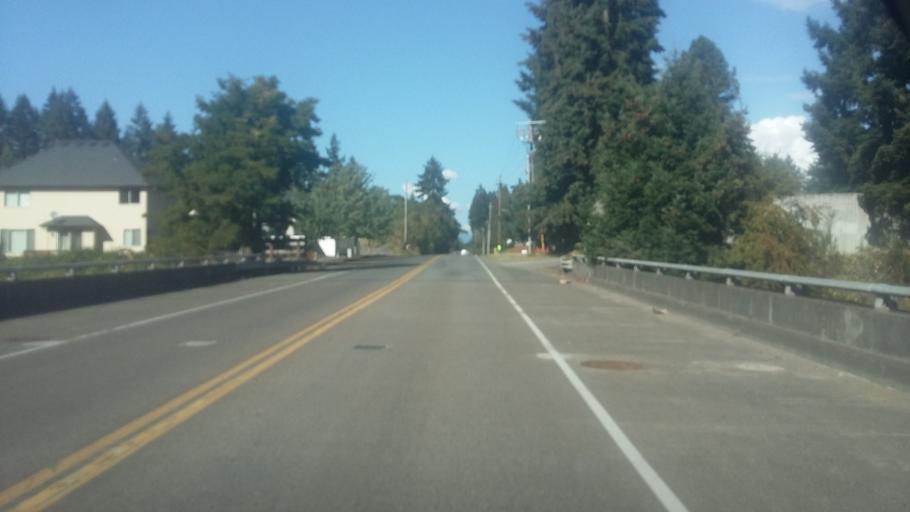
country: US
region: Washington
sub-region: Clark County
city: Barberton
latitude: 45.6993
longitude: -122.6205
